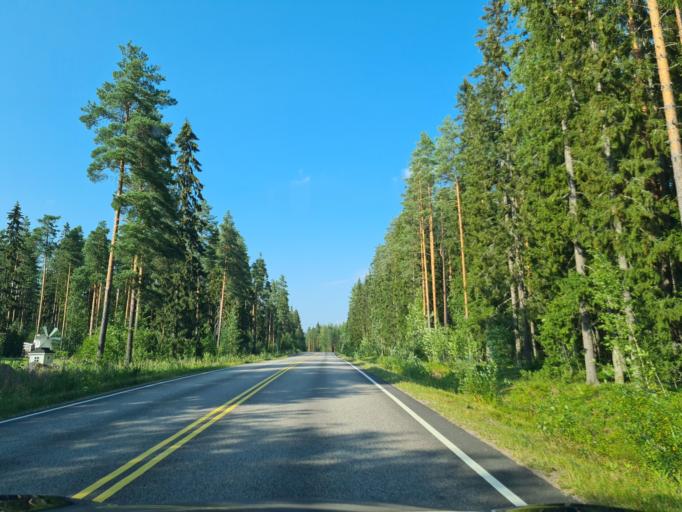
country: FI
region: Satakunta
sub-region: Pohjois-Satakunta
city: Karvia
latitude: 62.2017
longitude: 22.5980
